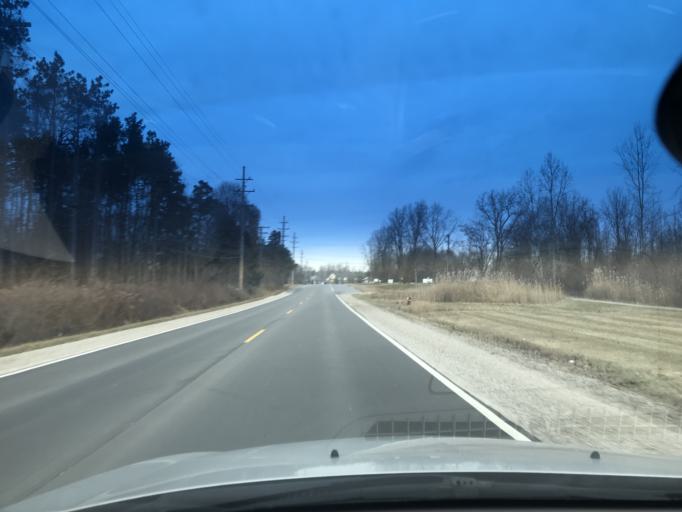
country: US
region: Michigan
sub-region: Macomb County
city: Shelby
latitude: 42.7072
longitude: -83.0548
